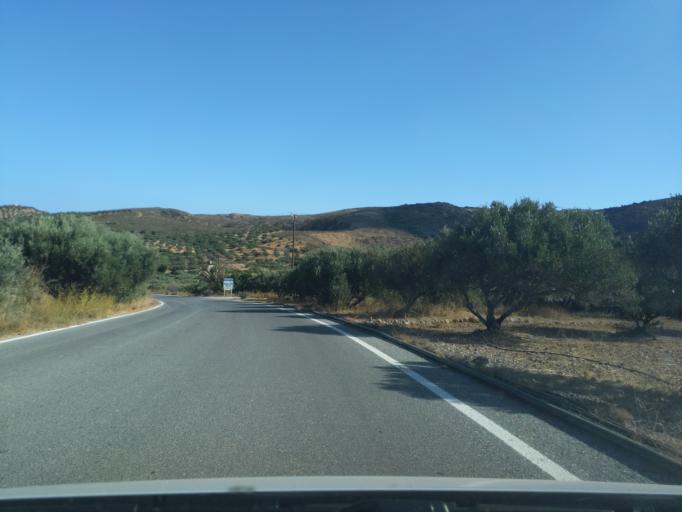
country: GR
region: Crete
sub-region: Nomos Lasithiou
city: Palekastro
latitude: 35.2207
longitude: 26.2588
